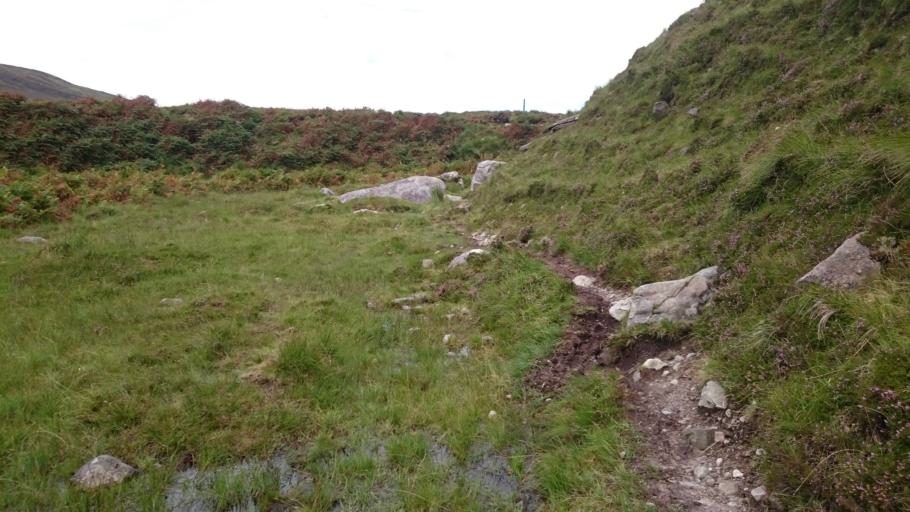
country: IE
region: Connaught
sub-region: Maigh Eo
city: Westport
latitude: 53.9894
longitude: -9.5855
